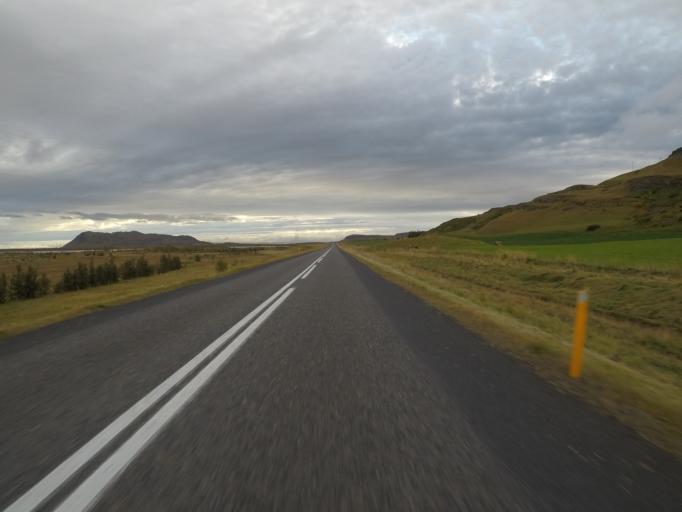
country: IS
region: South
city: Vestmannaeyjar
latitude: 64.0676
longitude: -20.0559
